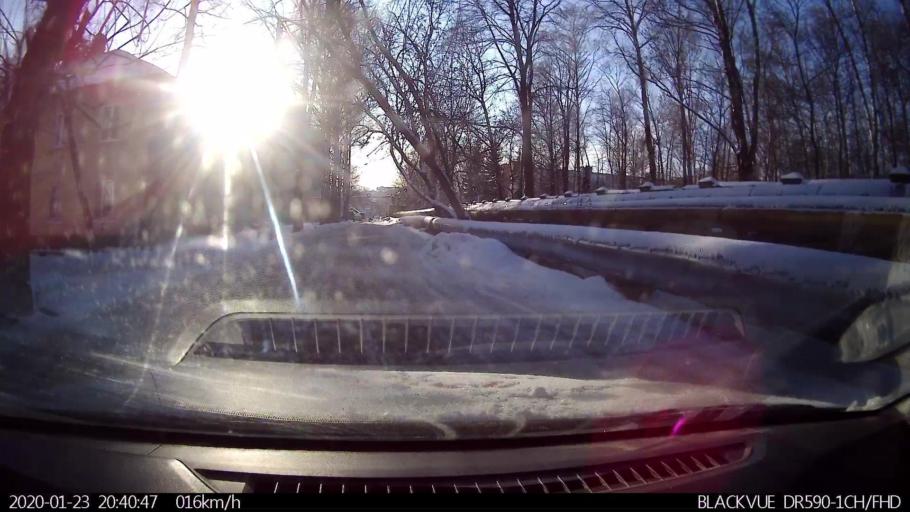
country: RU
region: Nizjnij Novgorod
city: Nizhniy Novgorod
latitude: 56.3000
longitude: 43.9971
